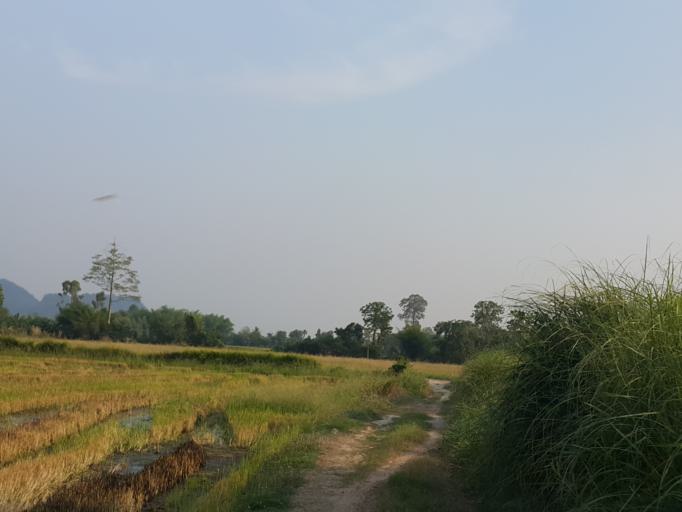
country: TH
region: Uthai Thani
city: Huai Khot
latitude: 15.3132
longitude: 99.6736
